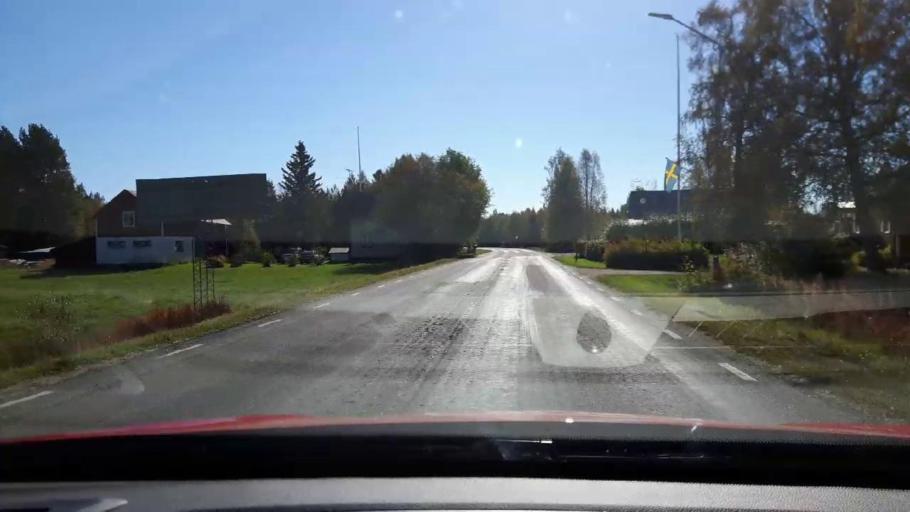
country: SE
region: Jaemtland
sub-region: Harjedalens Kommun
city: Sveg
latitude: 62.3113
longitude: 14.0393
